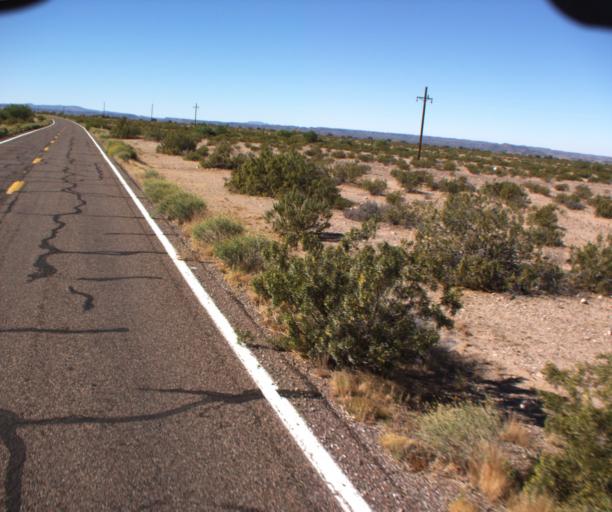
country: US
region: Arizona
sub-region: Maricopa County
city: Gila Bend
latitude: 32.6907
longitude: -112.8531
